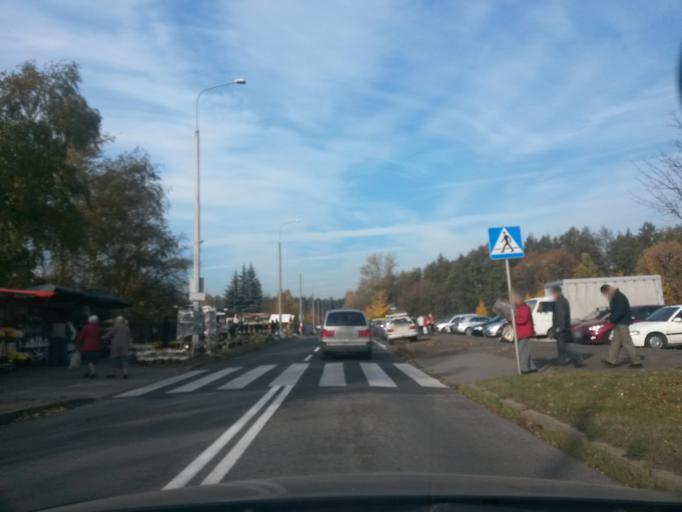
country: PL
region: Greater Poland Voivodeship
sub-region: Powiat poznanski
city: Plewiska
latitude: 52.3901
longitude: 16.8306
